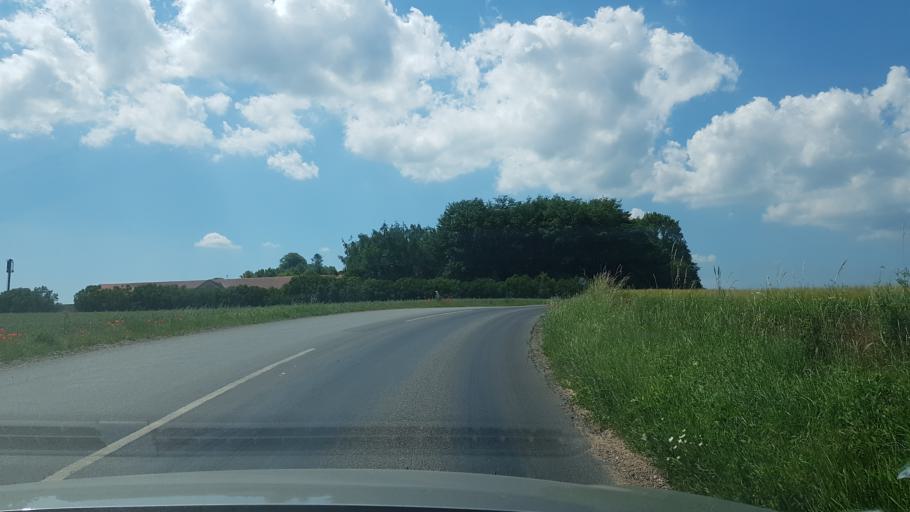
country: DK
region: Zealand
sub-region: Kalundborg Kommune
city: Svebolle
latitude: 55.6820
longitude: 11.2252
